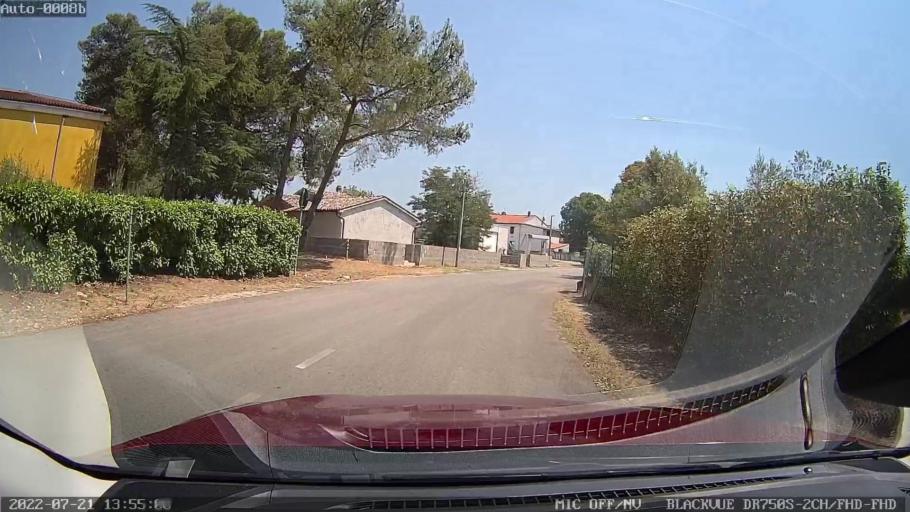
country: HR
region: Istarska
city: Pazin
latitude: 45.1217
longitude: 13.8359
